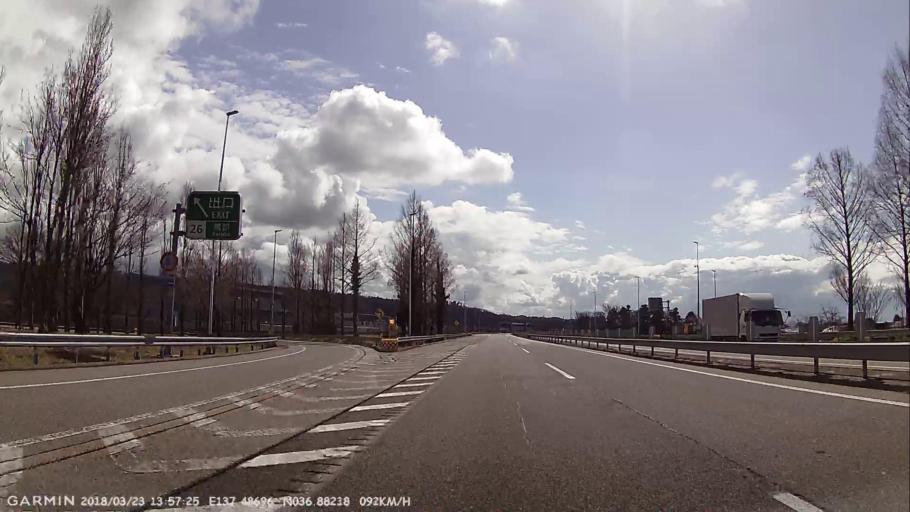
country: JP
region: Toyama
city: Nyuzen
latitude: 36.8820
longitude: 137.4868
